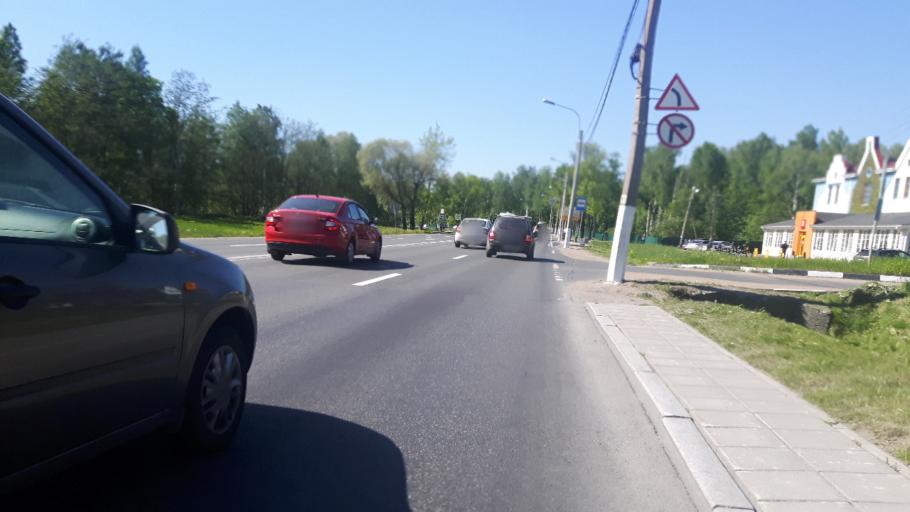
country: RU
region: Leningrad
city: Gorbunki
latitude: 59.8702
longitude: 29.9713
